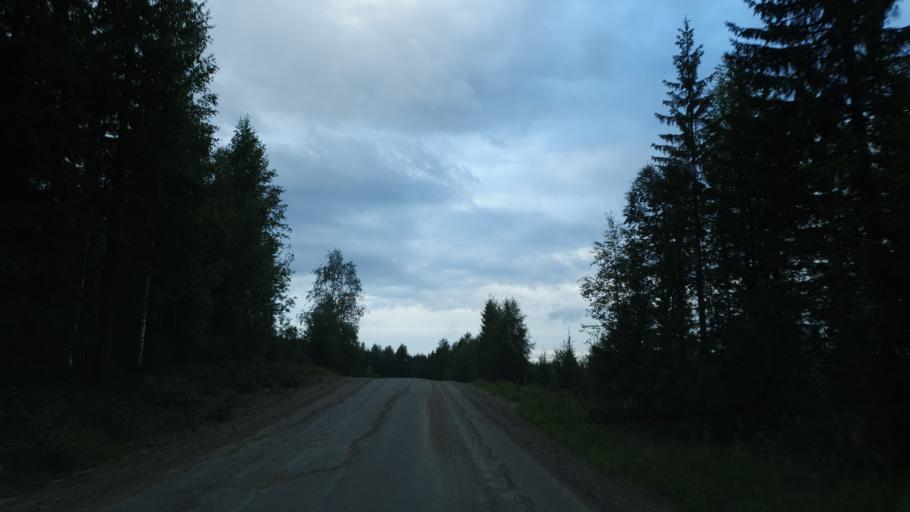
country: FI
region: Kainuu
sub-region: Kehys-Kainuu
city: Kuhmo
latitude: 64.2023
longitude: 29.3713
